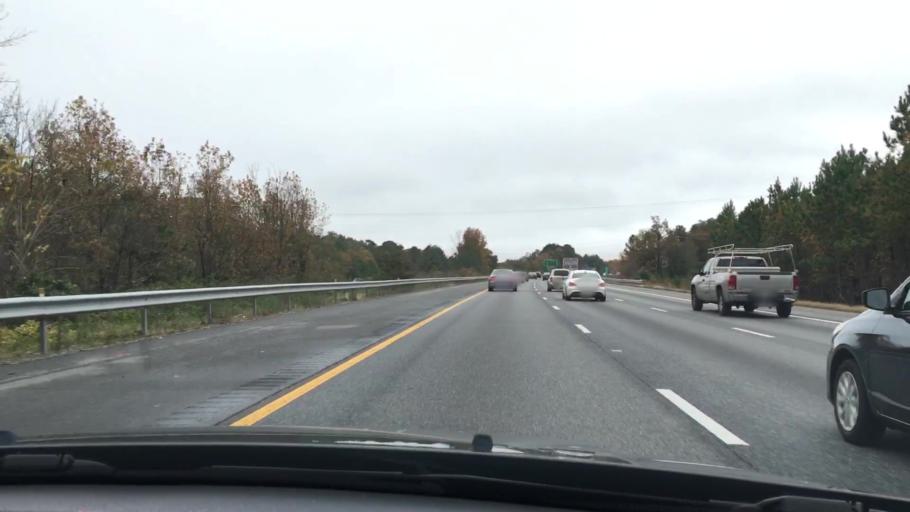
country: US
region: Virginia
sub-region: Hanover County
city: Ashland
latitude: 37.8621
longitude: -77.4536
